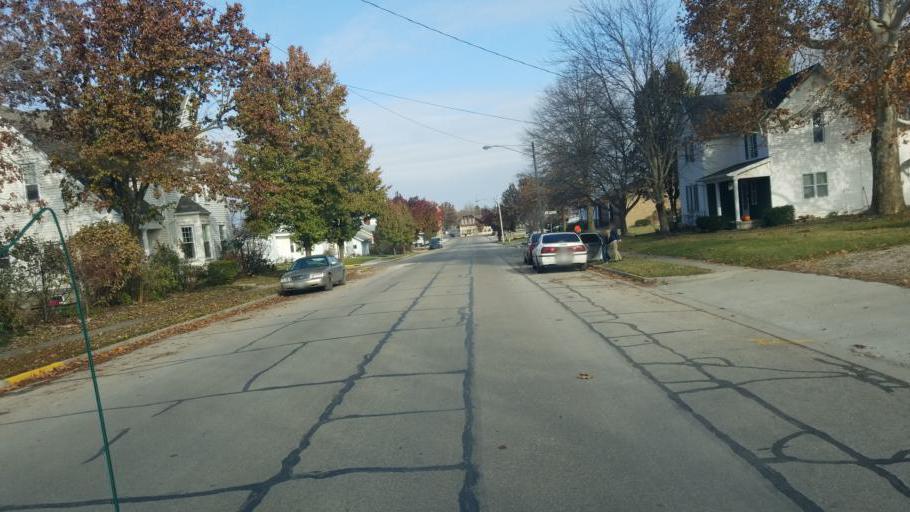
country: US
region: Indiana
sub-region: Adams County
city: Berne
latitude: 40.6554
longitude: -84.9513
